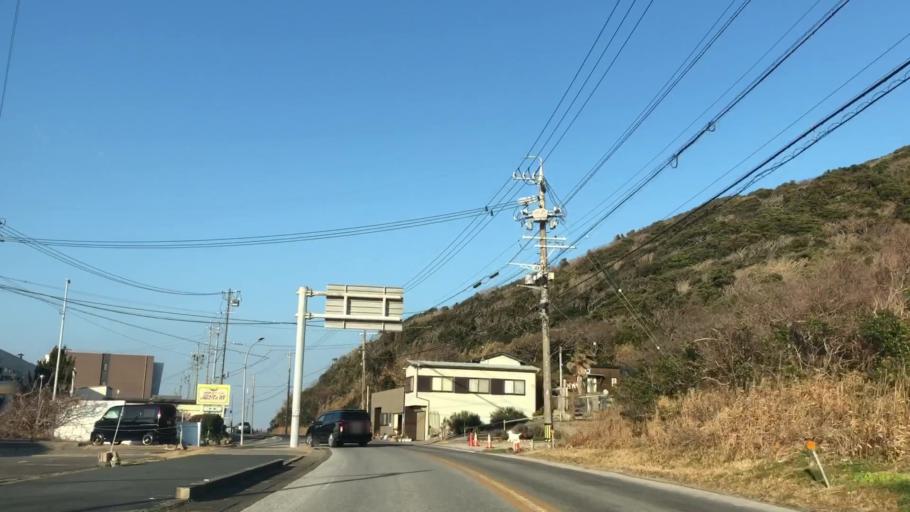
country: JP
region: Aichi
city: Toyohama
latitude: 34.5842
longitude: 137.0252
